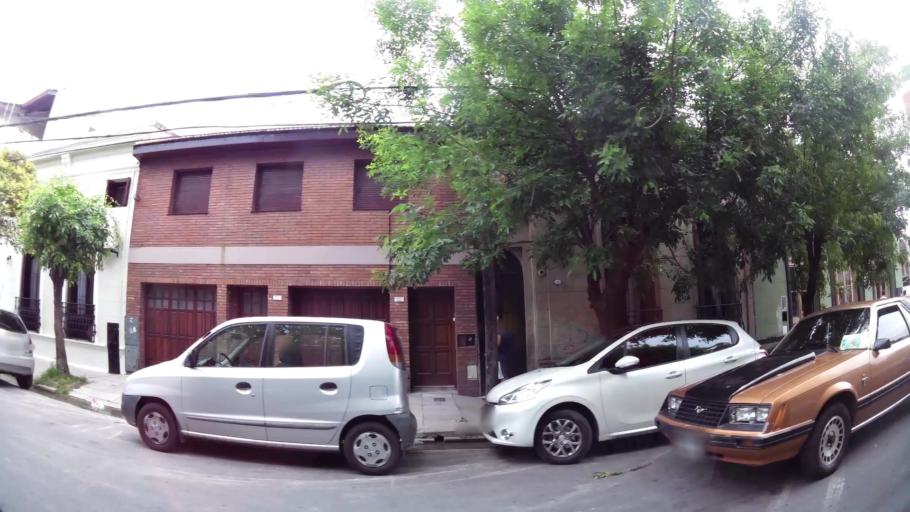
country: AR
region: Buenos Aires
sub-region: Partido de Avellaneda
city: Avellaneda
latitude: -34.6647
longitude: -58.3691
